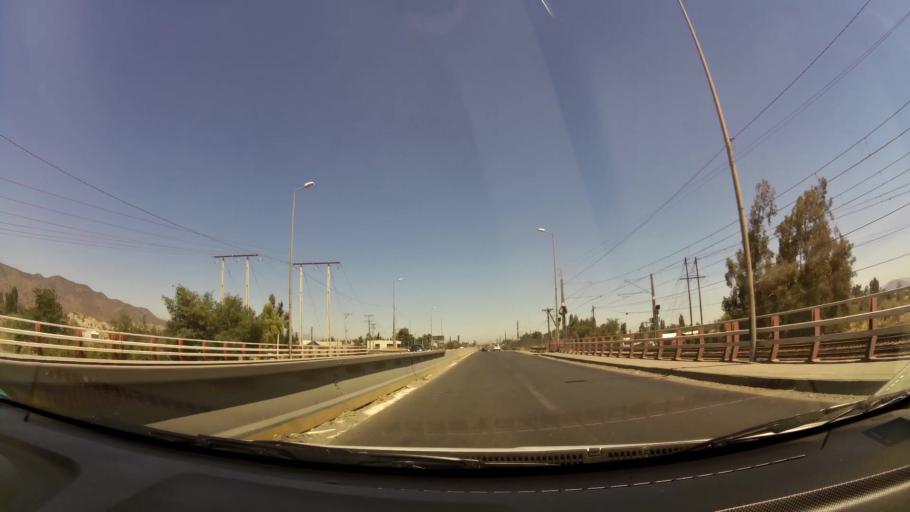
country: CL
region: O'Higgins
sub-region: Provincia de Cachapoal
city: Rancagua
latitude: -34.1947
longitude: -70.7560
